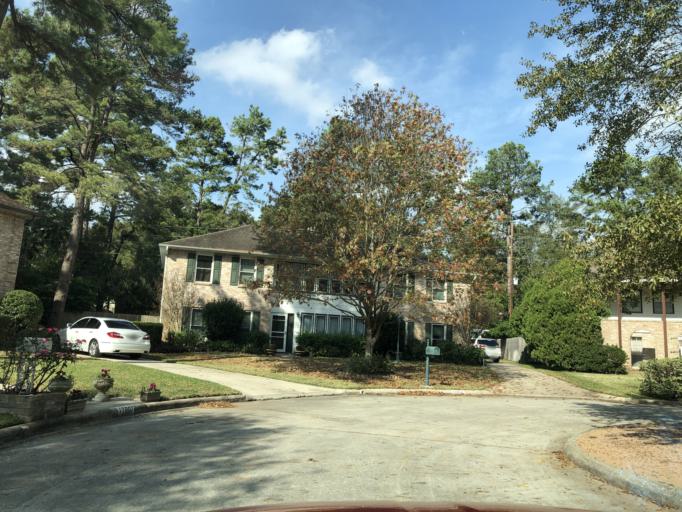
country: US
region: Texas
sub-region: Harris County
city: Tomball
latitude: 30.0254
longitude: -95.5471
